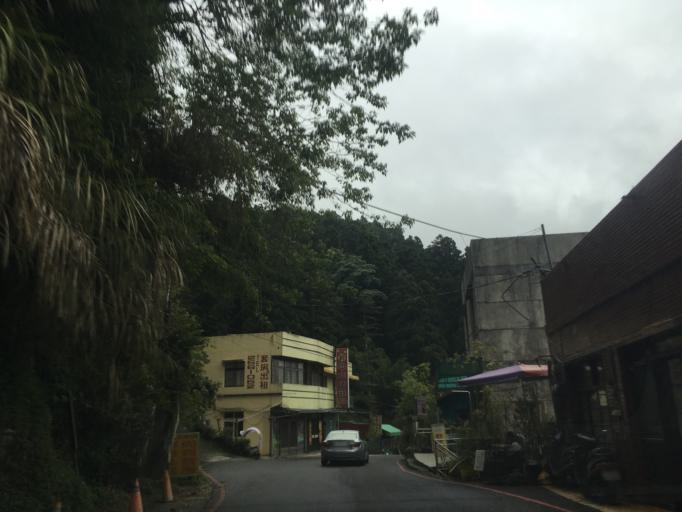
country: TW
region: Taiwan
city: Lugu
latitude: 23.5051
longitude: 120.6969
